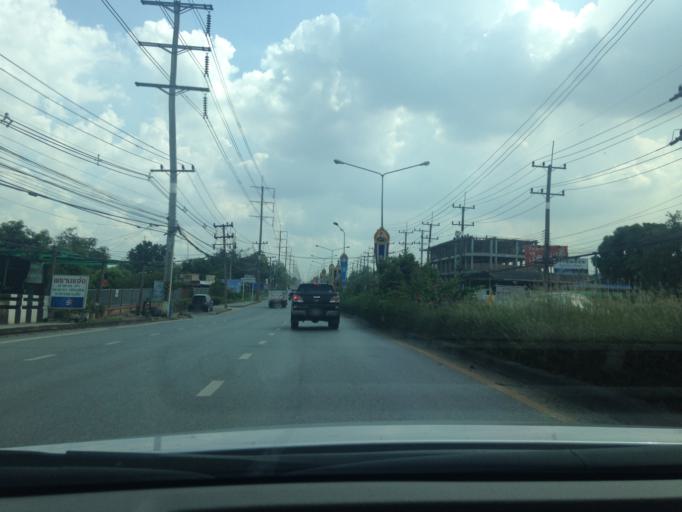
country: TH
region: Pathum Thani
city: Sam Khok
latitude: 14.0597
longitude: 100.5238
